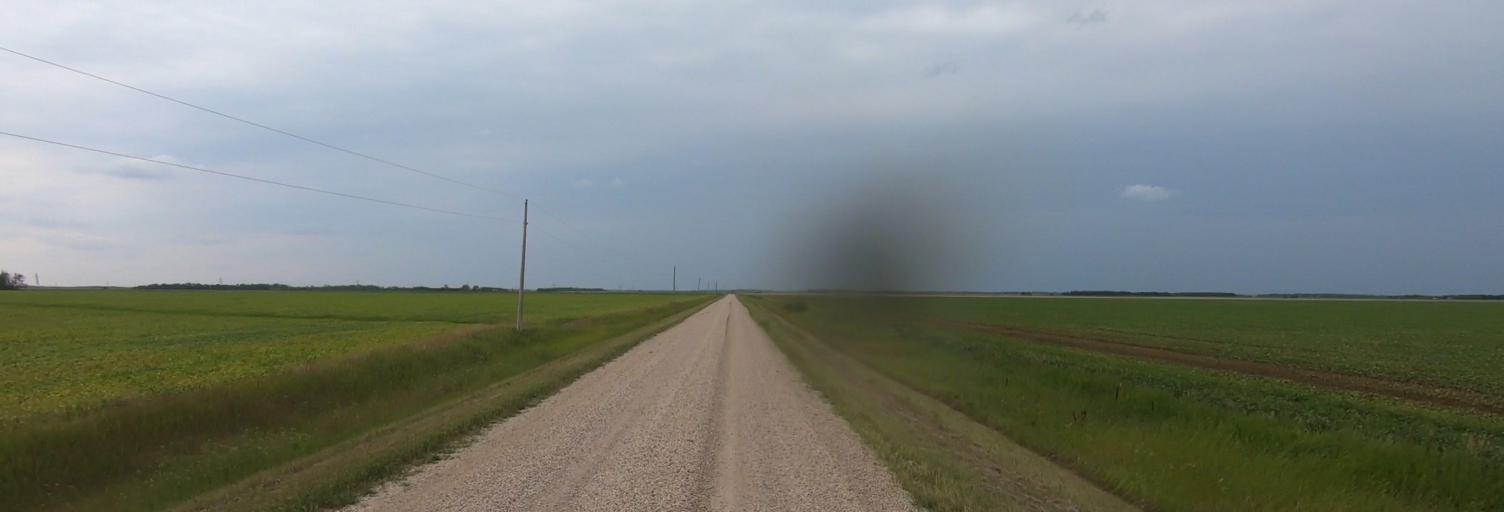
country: CA
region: Manitoba
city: Headingley
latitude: 49.7300
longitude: -97.4136
